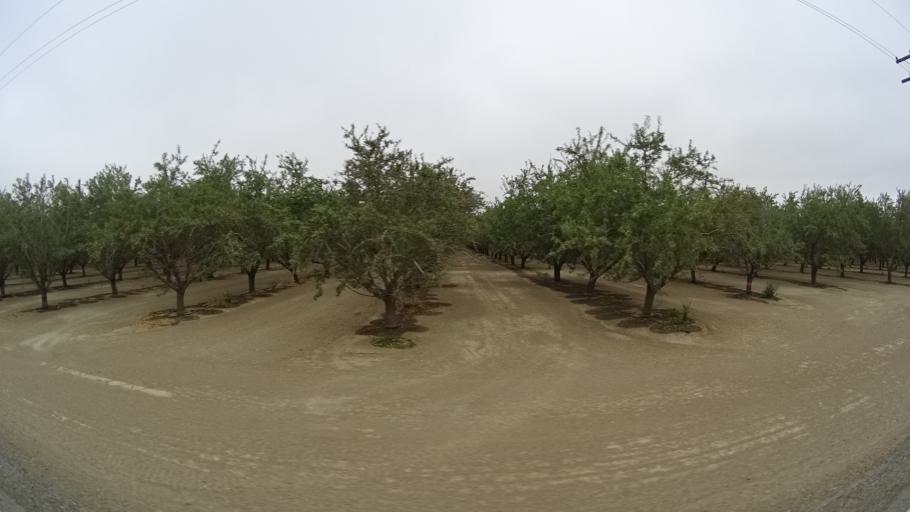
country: US
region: California
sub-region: Yolo County
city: Dunnigan
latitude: 38.9255
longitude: -121.9827
